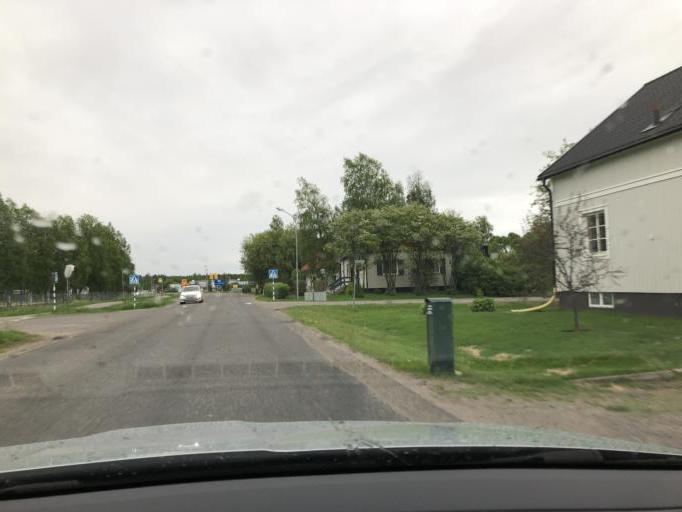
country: SE
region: Norrbotten
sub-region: Pitea Kommun
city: Bergsviken
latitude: 65.3404
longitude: 21.4019
